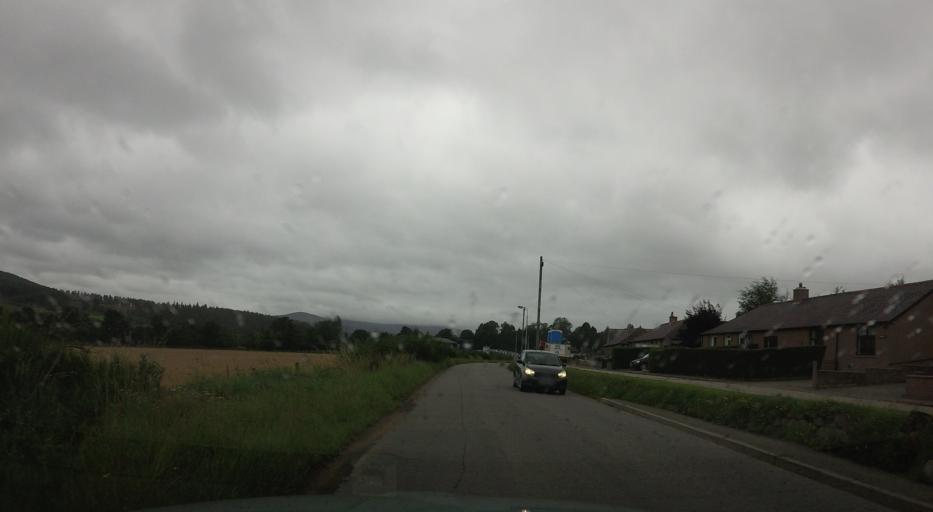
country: GB
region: Scotland
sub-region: Aberdeenshire
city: Banchory
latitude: 57.0212
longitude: -2.5330
